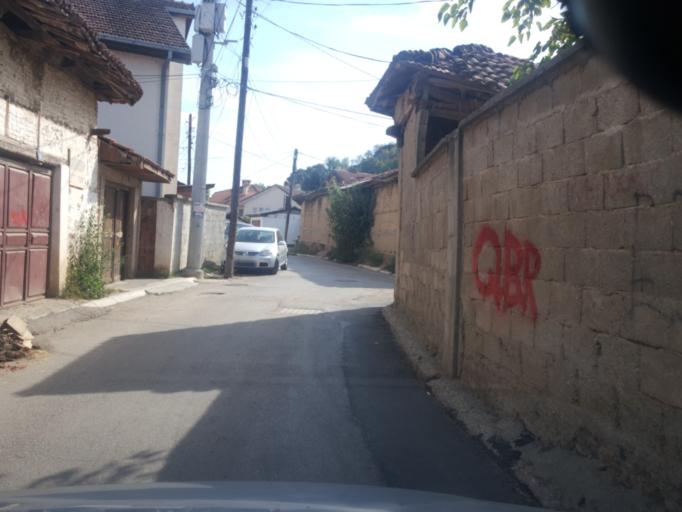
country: XK
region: Gjakova
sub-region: Komuna e Gjakoves
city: Gjakove
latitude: 42.3833
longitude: 20.4233
